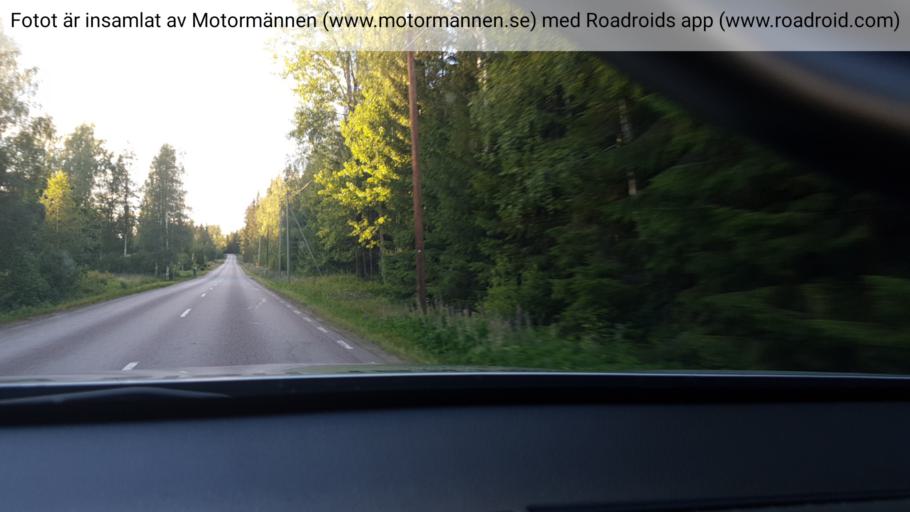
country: SE
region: Vaermland
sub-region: Torsby Kommun
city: Torsby
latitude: 60.0891
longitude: 13.0881
